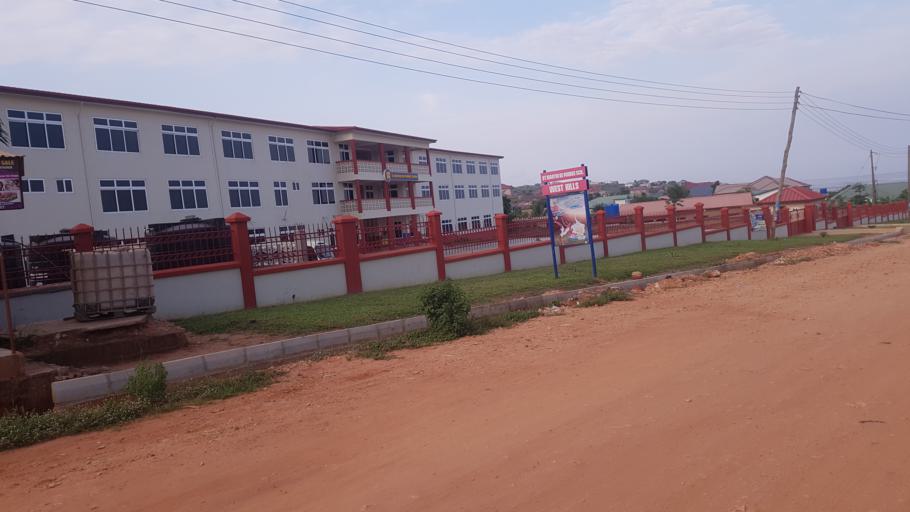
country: GH
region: Greater Accra
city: Gbawe
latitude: 5.5242
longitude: -0.3473
